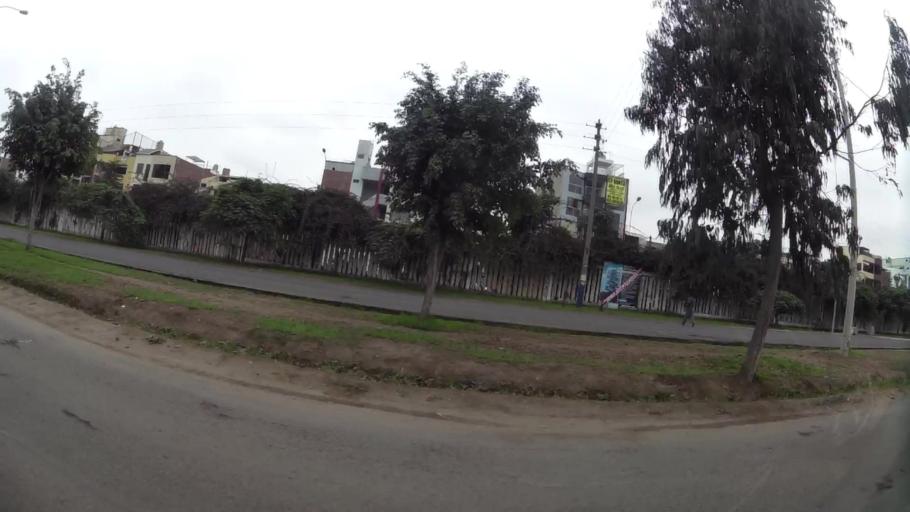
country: PE
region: Lima
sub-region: Lima
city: La Molina
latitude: -12.0607
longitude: -76.9382
